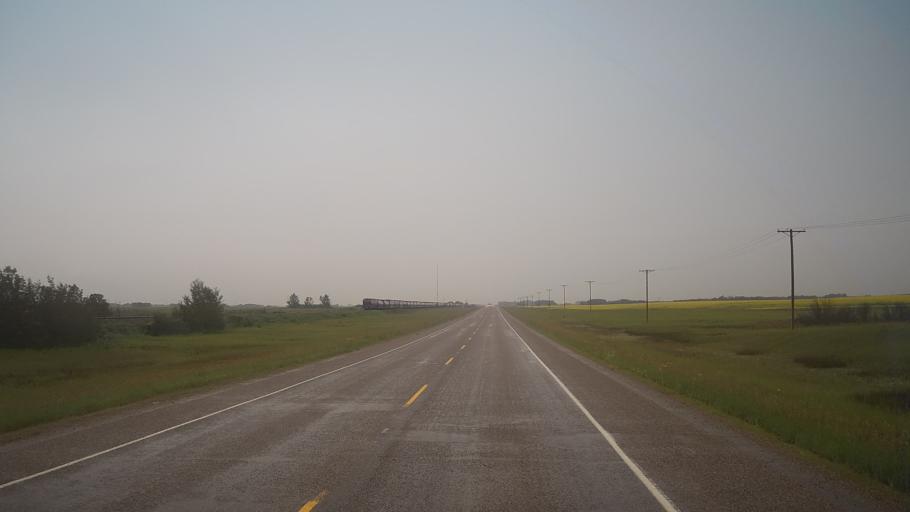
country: CA
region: Saskatchewan
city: Biggar
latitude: 52.1649
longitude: -108.2987
